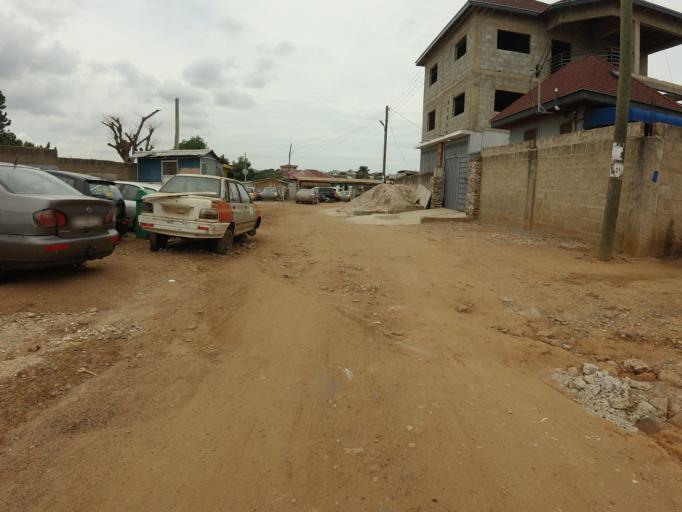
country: GH
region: Greater Accra
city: Dome
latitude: 5.6050
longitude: -0.2230
